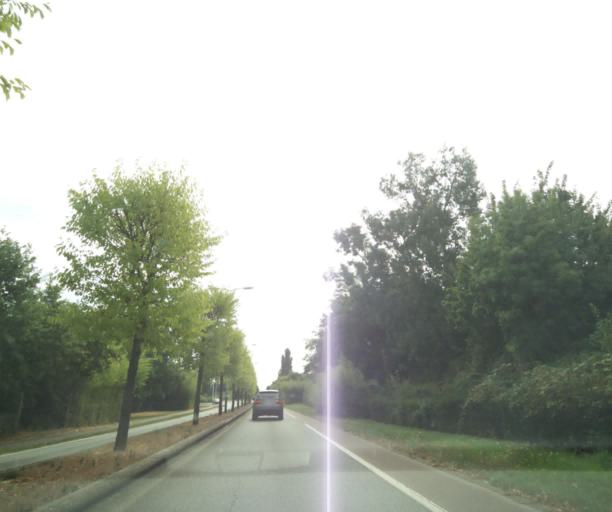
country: FR
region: Pays de la Loire
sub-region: Departement de la Loire-Atlantique
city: Saint-Herblain
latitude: 47.2155
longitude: -1.6400
